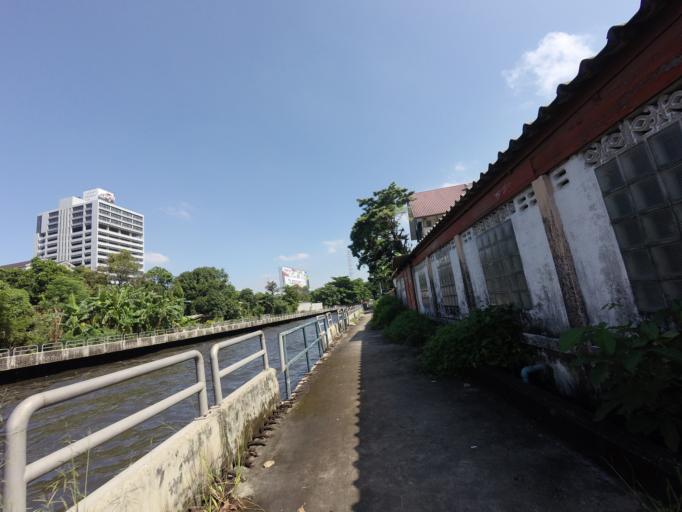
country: TH
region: Bangkok
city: Watthana
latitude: 13.7464
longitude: 100.6000
